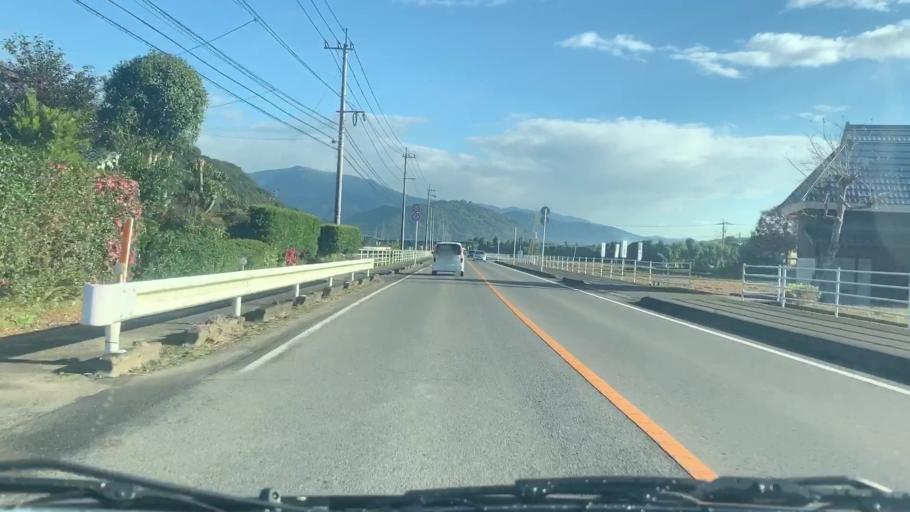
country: JP
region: Saga Prefecture
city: Takeocho-takeo
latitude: 33.2538
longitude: 130.0759
